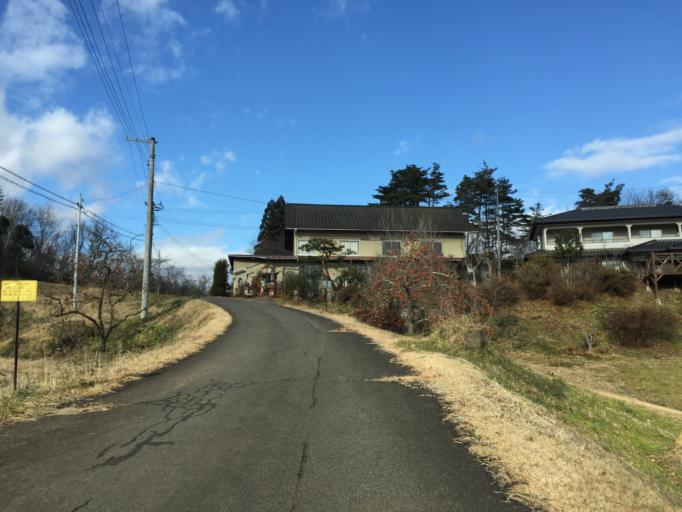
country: JP
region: Fukushima
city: Fukushima-shi
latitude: 37.6763
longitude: 140.4890
